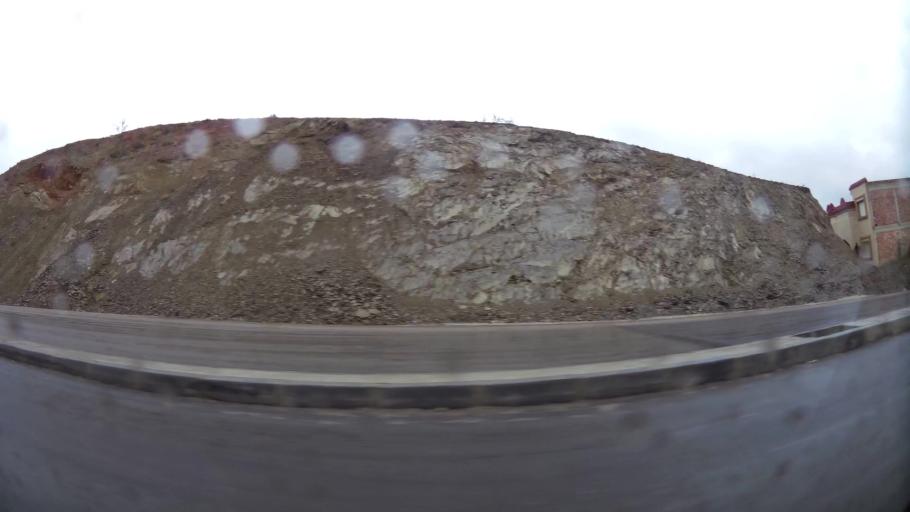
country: MA
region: Taza-Al Hoceima-Taounate
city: Imzourene
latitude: 35.0210
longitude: -3.8202
